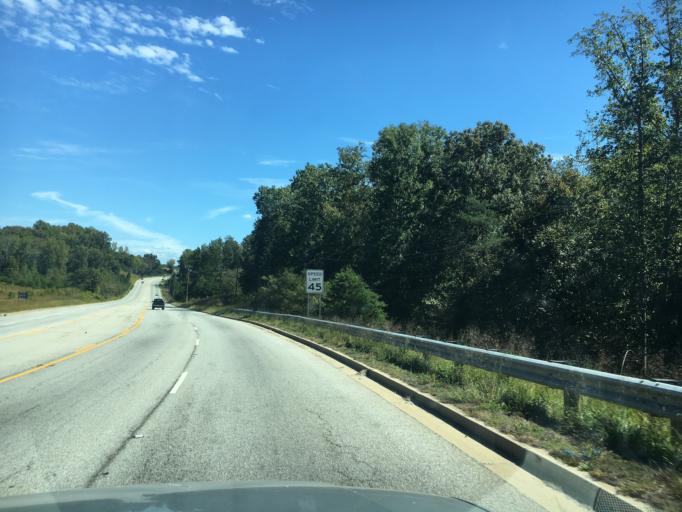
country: US
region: South Carolina
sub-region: Spartanburg County
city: Roebuck
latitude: 34.9047
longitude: -81.9430
